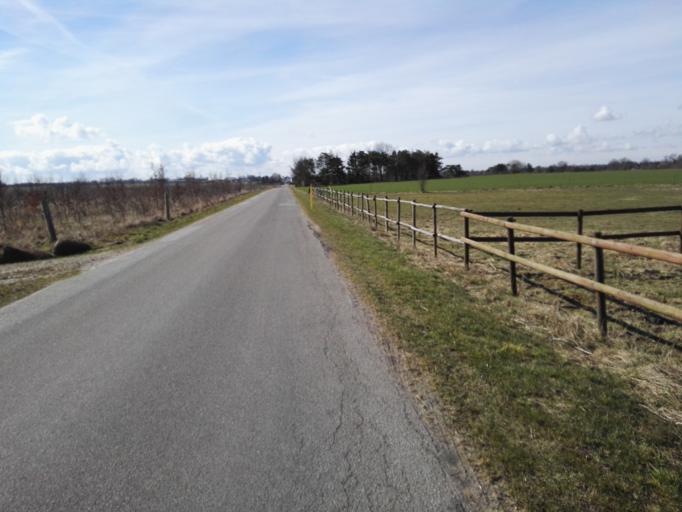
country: DK
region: Zealand
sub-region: Lejre Kommune
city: Ejby
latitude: 55.7801
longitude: 11.8296
